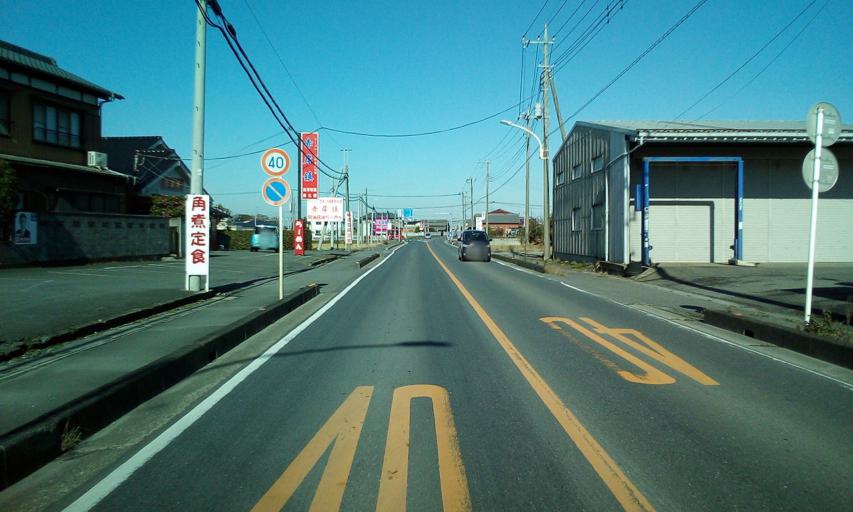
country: JP
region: Saitama
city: Yoshikawa
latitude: 35.9052
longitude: 139.8673
